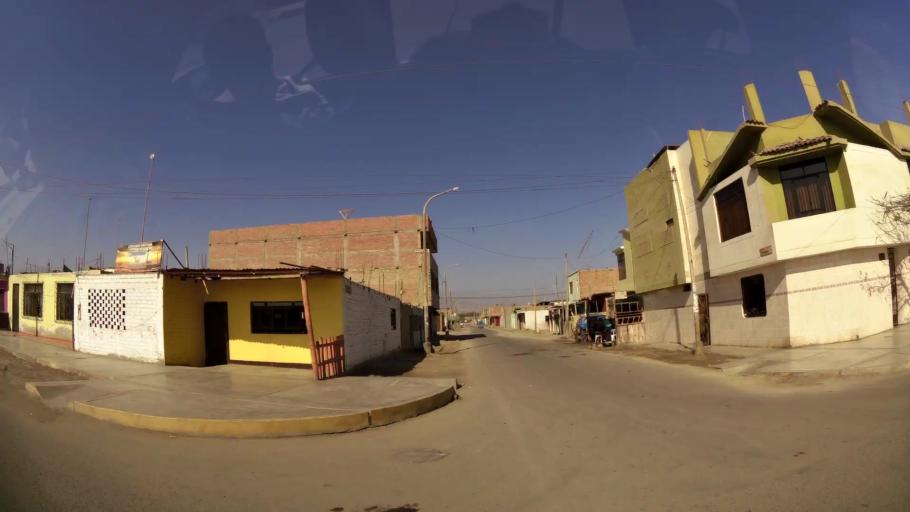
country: PE
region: Ica
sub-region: Provincia de Chincha
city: Chincha Alta
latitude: -13.4015
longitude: -76.1238
